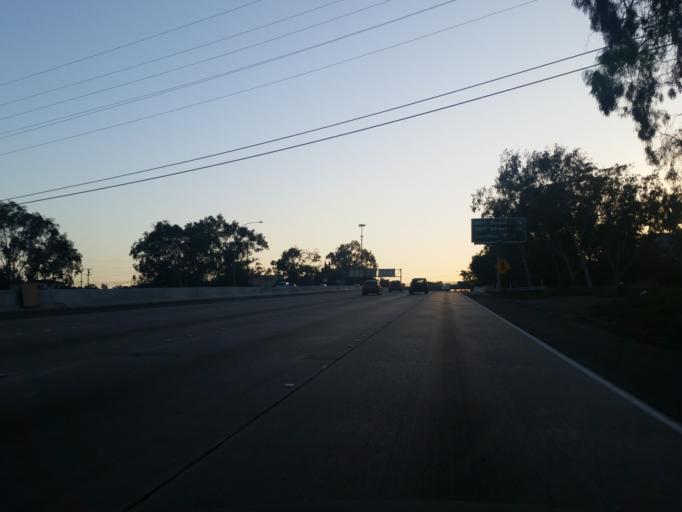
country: US
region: California
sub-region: San Diego County
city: San Diego
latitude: 32.7152
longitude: -117.1250
